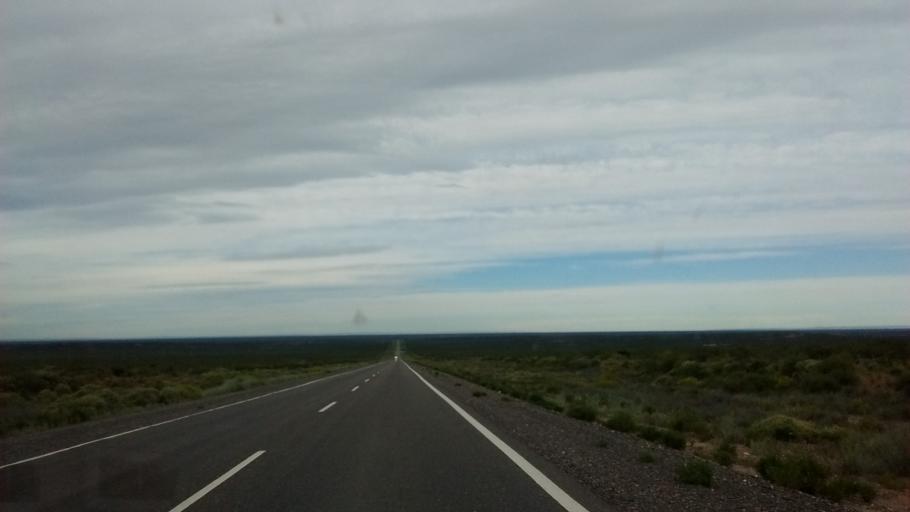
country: AR
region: Rio Negro
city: Contraalmirante Cordero
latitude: -38.4104
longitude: -68.0326
